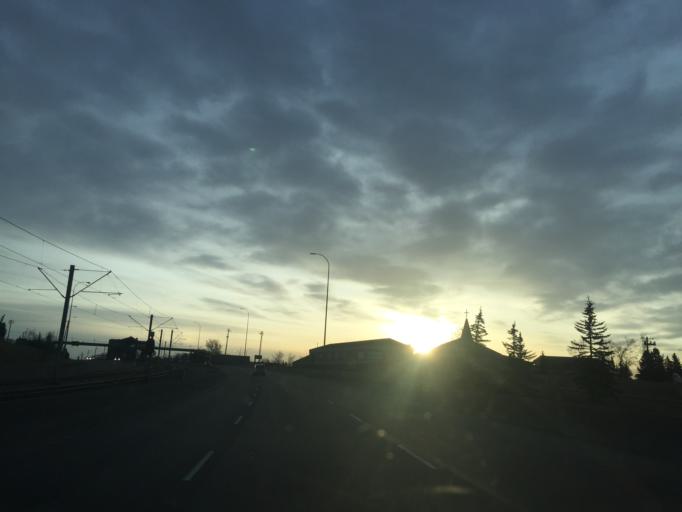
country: CA
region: Alberta
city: Calgary
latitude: 51.0454
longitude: -113.9988
